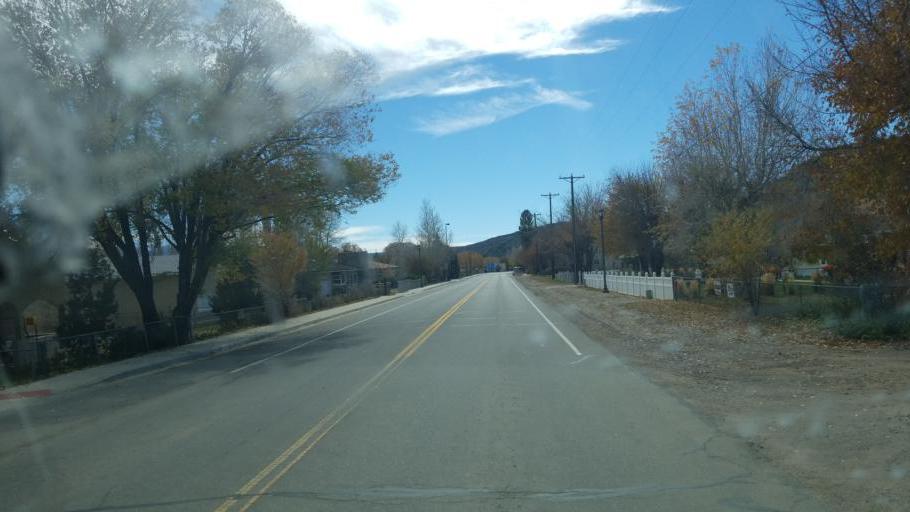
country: US
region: Colorado
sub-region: Costilla County
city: San Luis
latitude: 37.2042
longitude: -105.4253
